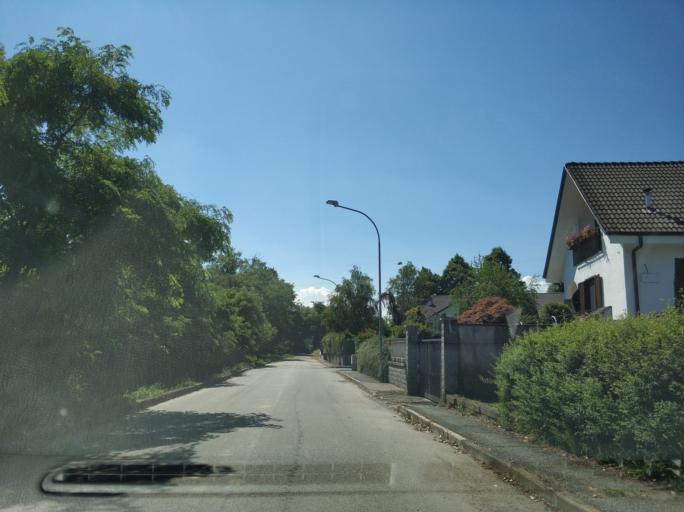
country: IT
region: Piedmont
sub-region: Provincia di Torino
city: San Benigno Canavese
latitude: 45.2285
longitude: 7.7721
